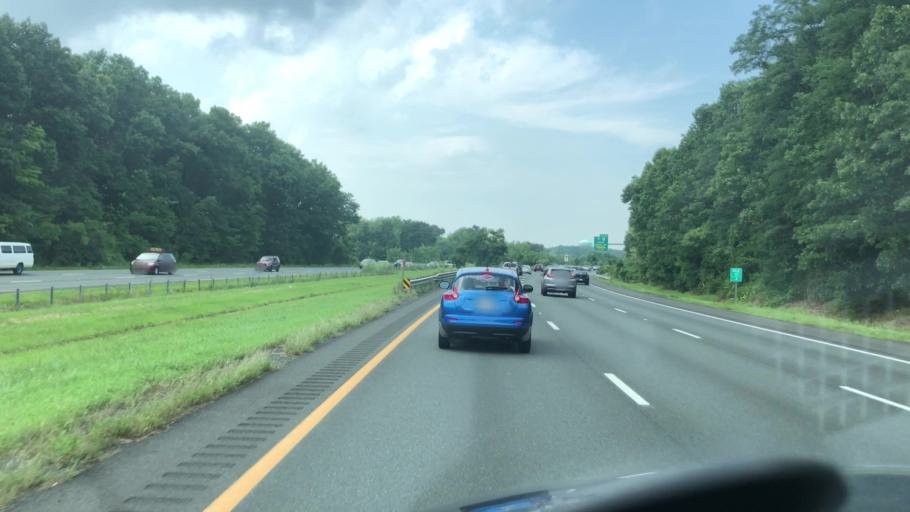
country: US
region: Massachusetts
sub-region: Hampden County
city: Chicopee
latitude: 42.1515
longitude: -72.6467
